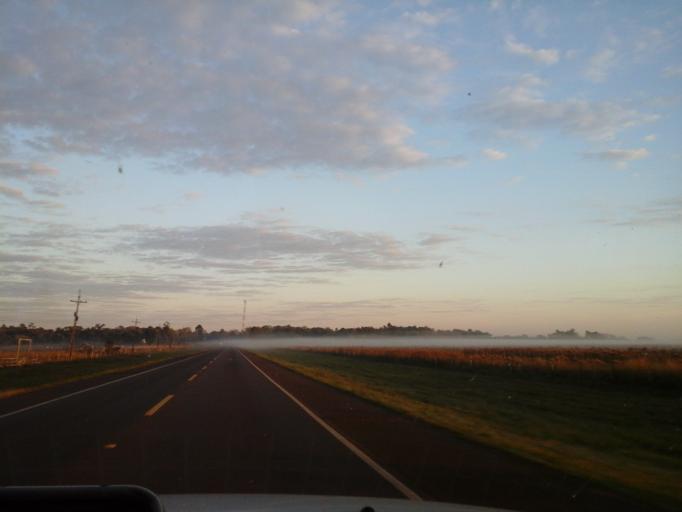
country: PY
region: Itapua
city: General Delgado
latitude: -27.0510
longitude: -56.6411
